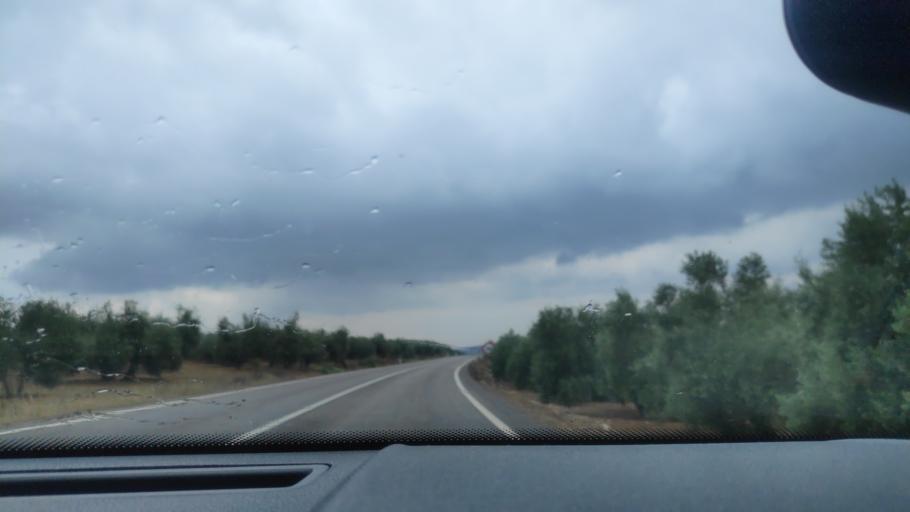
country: ES
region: Andalusia
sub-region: Provincia de Jaen
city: Jabalquinto
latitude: 38.0390
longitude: -3.7414
